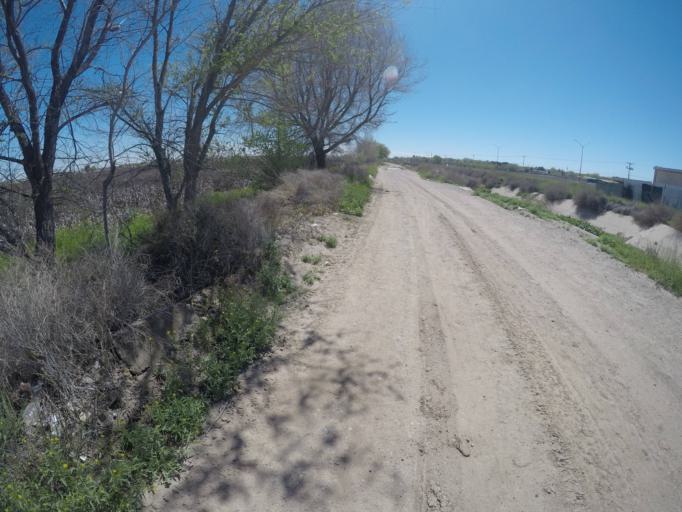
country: US
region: Texas
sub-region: El Paso County
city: Socorro Mission Number 1 Colonia
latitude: 31.6157
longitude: -106.3176
